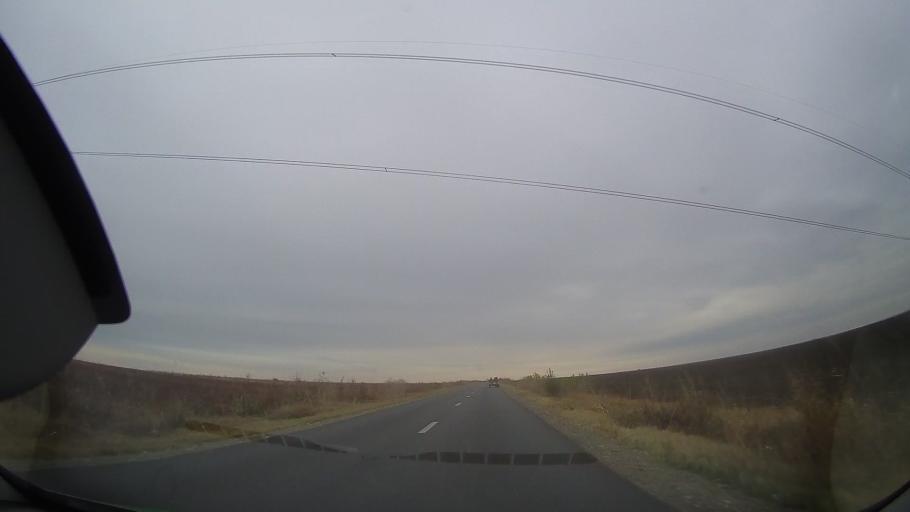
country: RO
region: Ialomita
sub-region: Oras Amara
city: Amara
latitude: 44.6405
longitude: 27.3007
